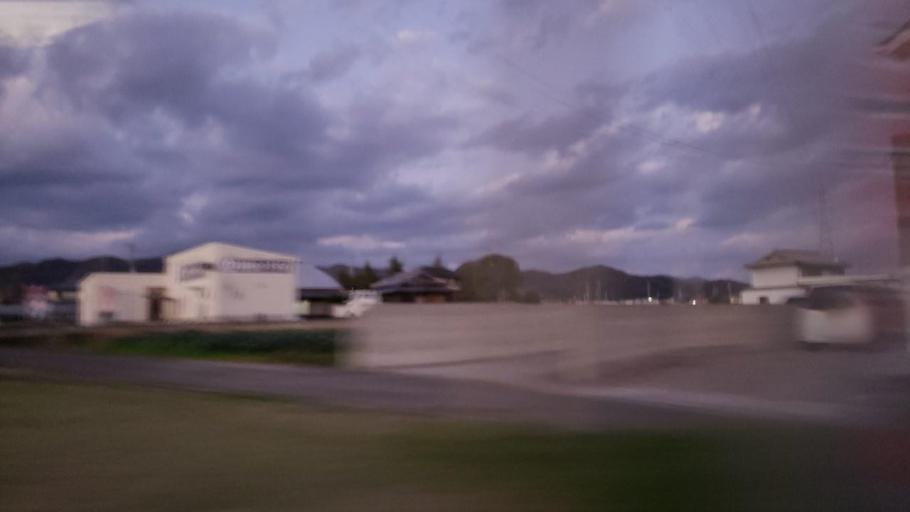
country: JP
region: Tokushima
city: Kamojimacho-jogejima
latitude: 34.0897
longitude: 134.2872
